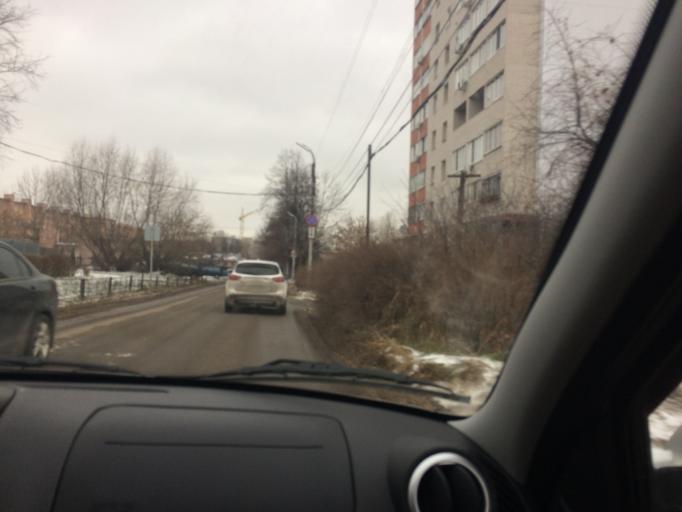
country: RU
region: Rjazan
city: Ryazan'
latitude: 54.6184
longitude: 39.7139
